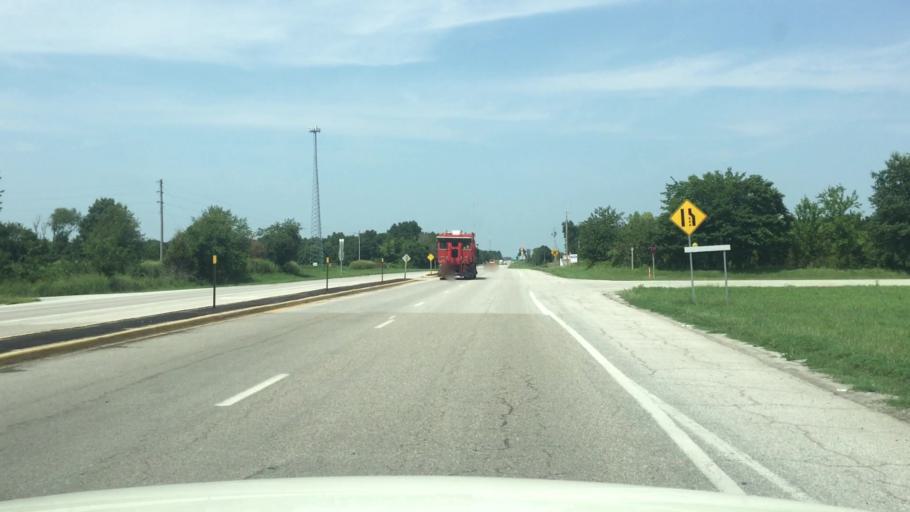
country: US
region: Kansas
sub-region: Cherokee County
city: Galena
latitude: 37.1783
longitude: -94.7043
